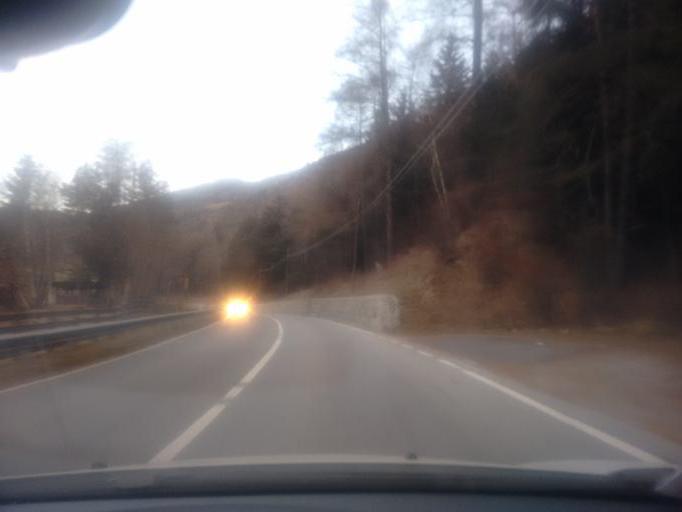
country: IT
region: Trentino-Alto Adige
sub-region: Bolzano
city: Campo di Trens
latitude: 46.8611
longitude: 11.5112
